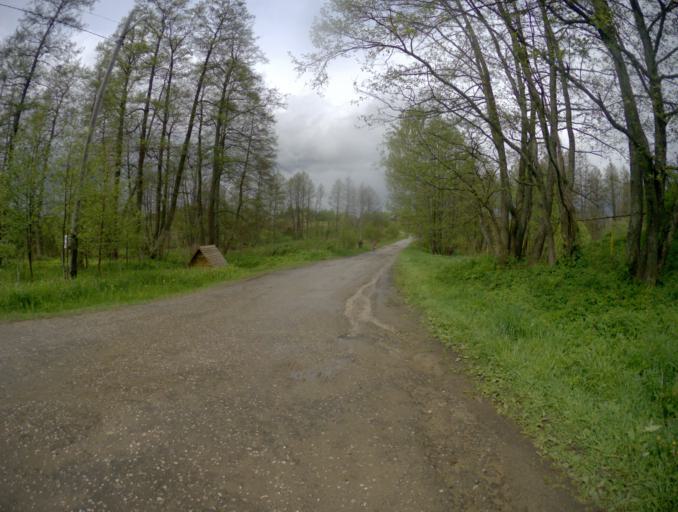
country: RU
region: Vladimir
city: Velikodvorskiy
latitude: 55.3703
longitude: 40.8599
